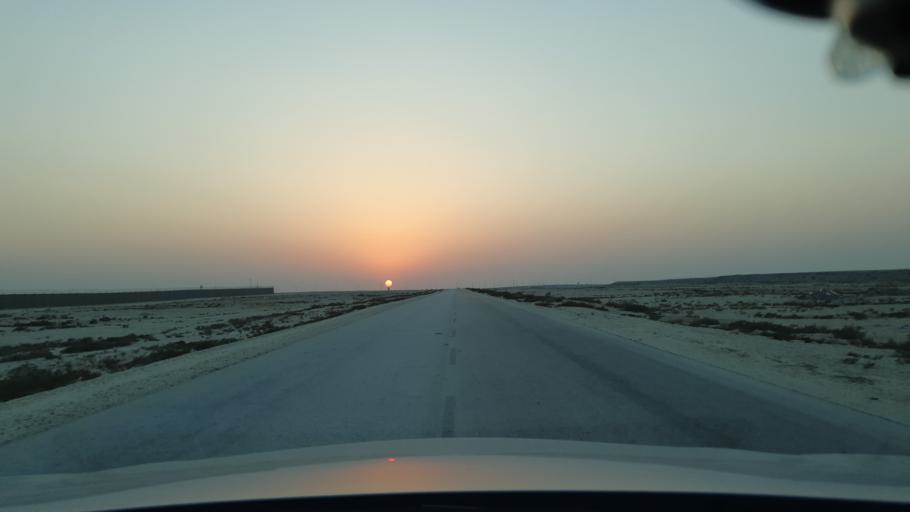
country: BH
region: Central Governorate
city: Dar Kulayb
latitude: 25.9558
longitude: 50.6053
